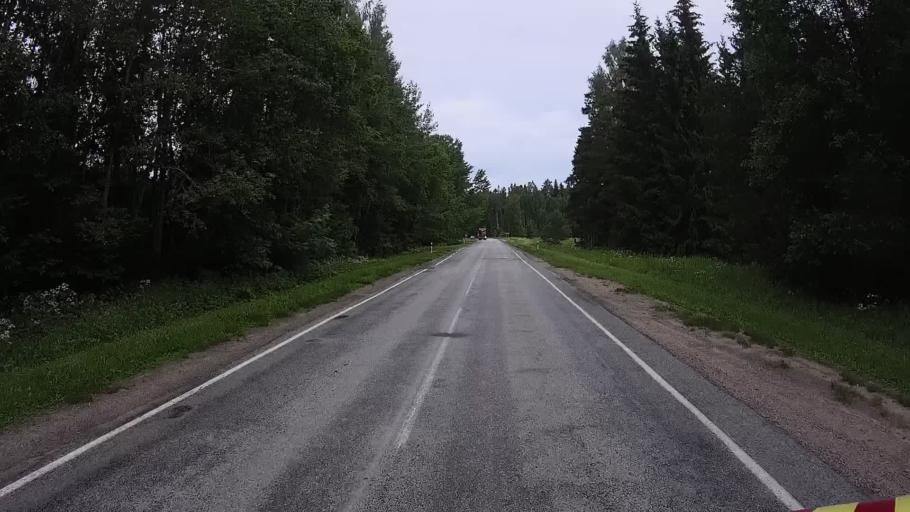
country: EE
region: Viljandimaa
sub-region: Karksi vald
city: Karksi-Nuia
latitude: 58.2157
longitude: 25.6197
